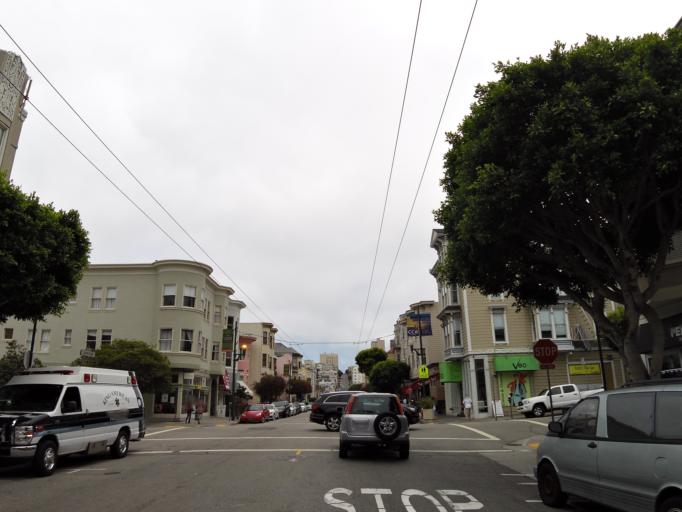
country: US
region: California
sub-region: San Francisco County
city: San Francisco
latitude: 37.7979
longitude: -122.4292
